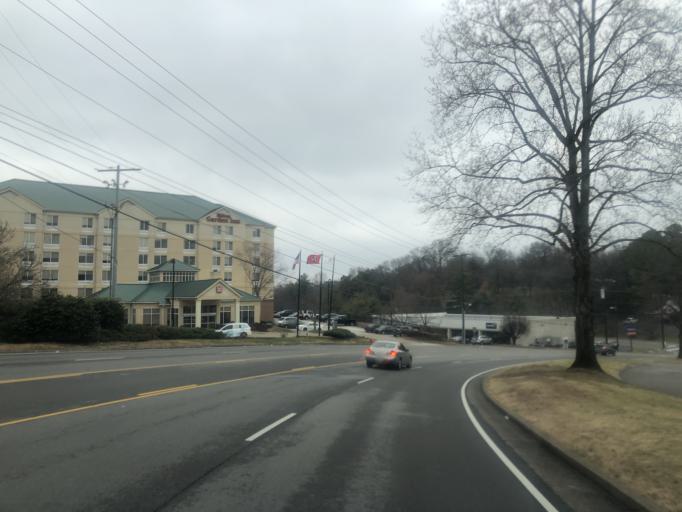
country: US
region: Tennessee
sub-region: Davidson County
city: Lakewood
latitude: 36.1504
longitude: -86.6766
